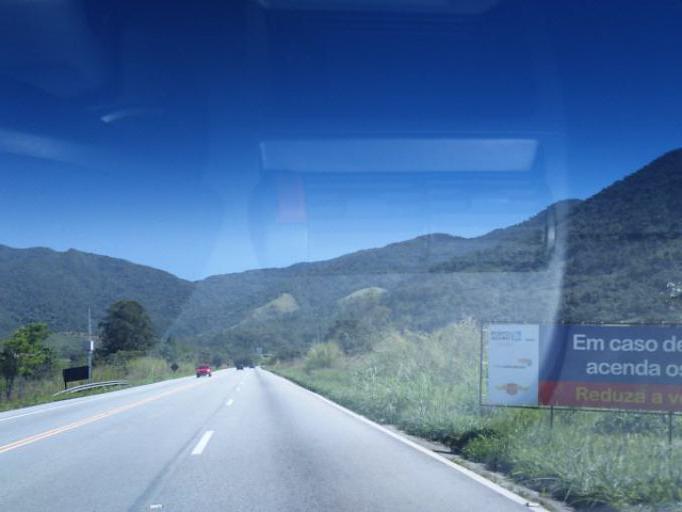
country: BR
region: Sao Paulo
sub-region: Tremembe
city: Tremembe
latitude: -22.8598
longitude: -45.6117
